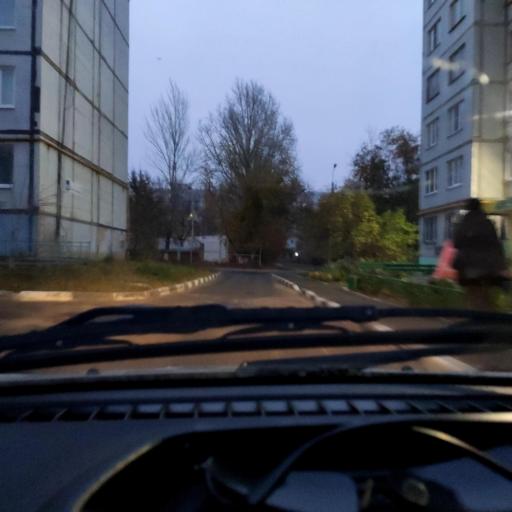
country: RU
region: Samara
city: Zhigulevsk
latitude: 53.4787
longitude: 49.4807
